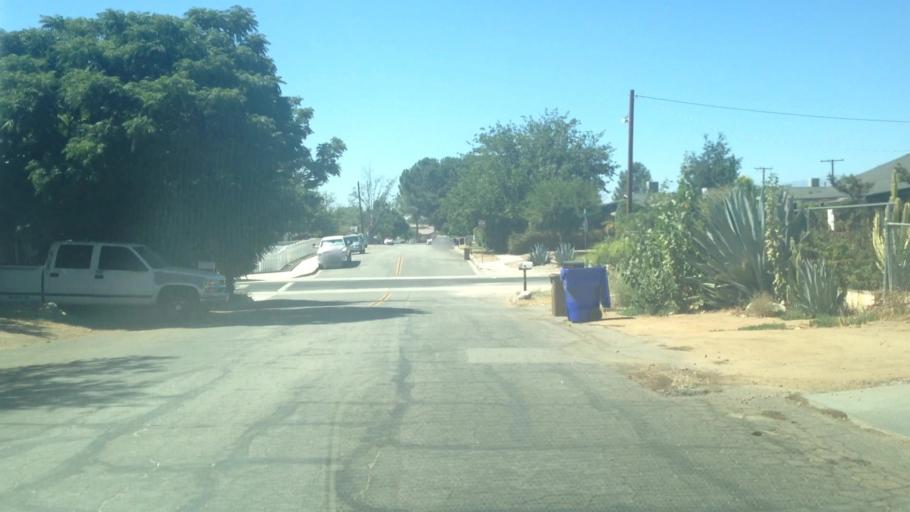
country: US
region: California
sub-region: San Bernardino County
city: Yucaipa
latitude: 34.0308
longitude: -117.0405
